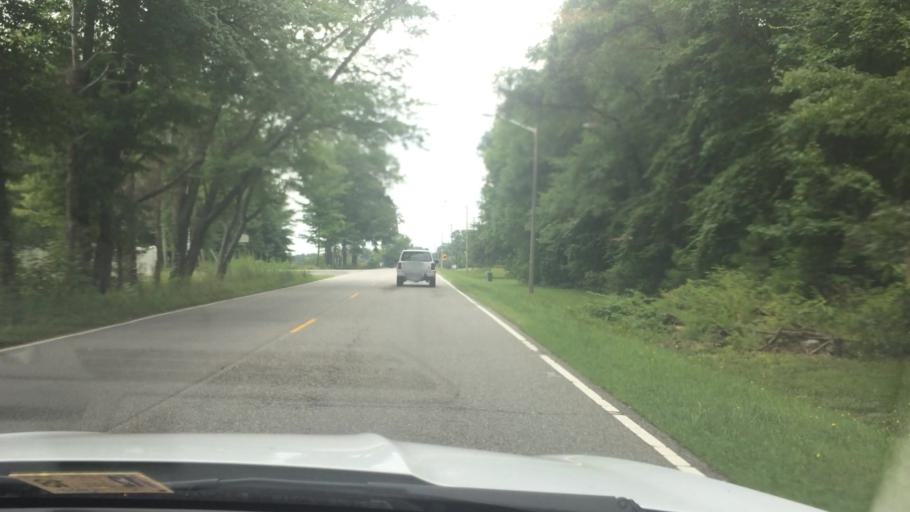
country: US
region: Virginia
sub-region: York County
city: Yorktown
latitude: 37.2159
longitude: -76.5689
